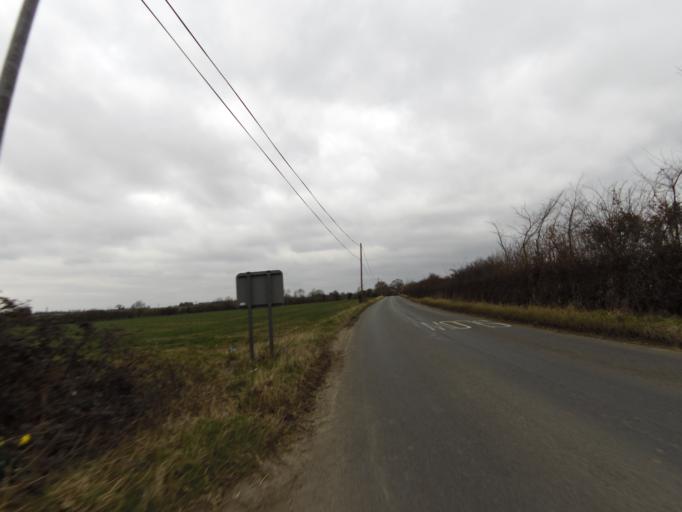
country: GB
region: England
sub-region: Suffolk
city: Ipswich
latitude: 52.1307
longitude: 1.1657
